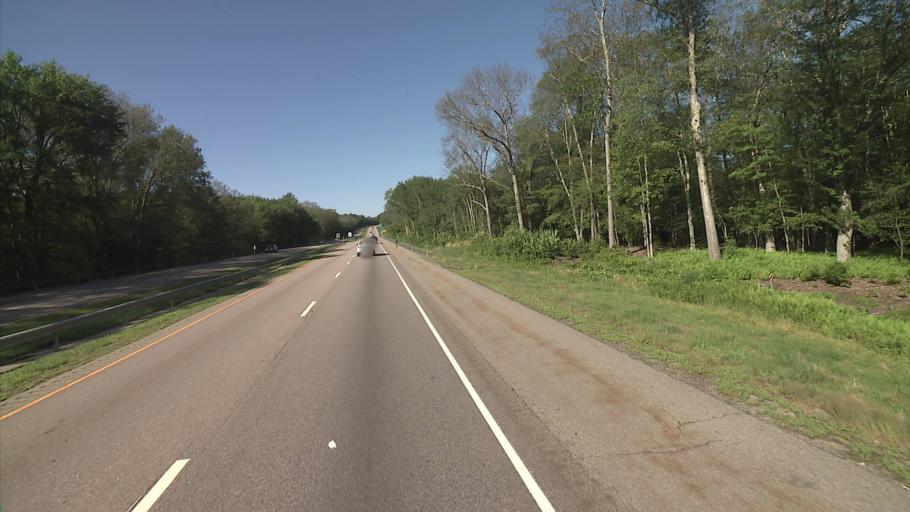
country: US
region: Connecticut
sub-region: New London County
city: Oxoboxo River
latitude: 41.4111
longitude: -72.1421
